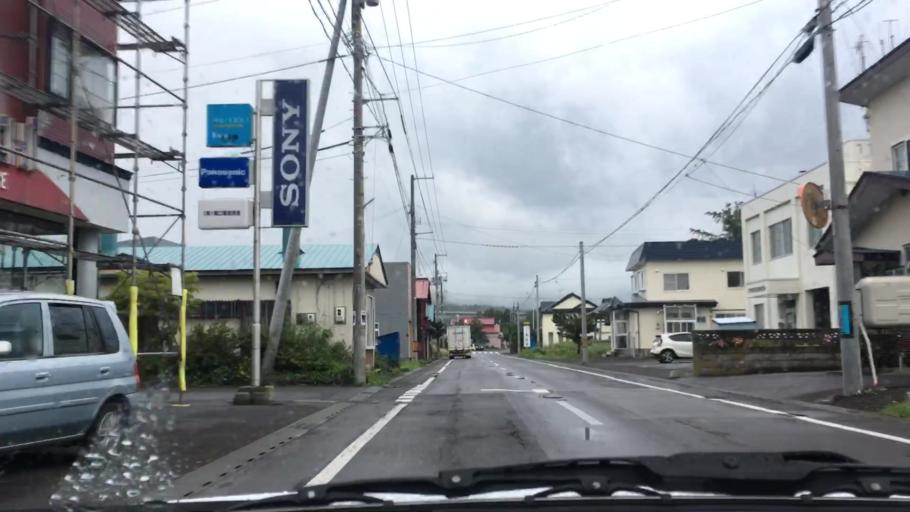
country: JP
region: Hokkaido
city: Nanae
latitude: 42.1886
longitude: 140.4246
